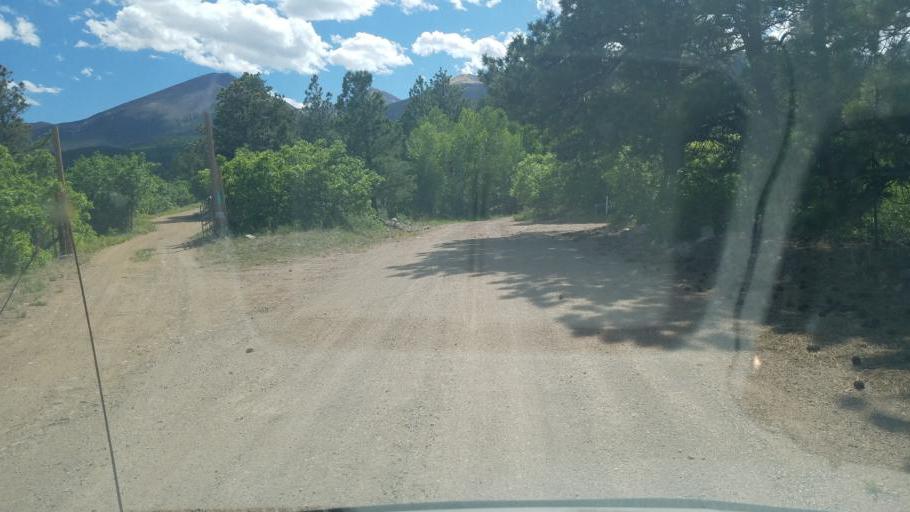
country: US
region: Colorado
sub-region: Custer County
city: Westcliffe
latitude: 38.2251
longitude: -105.6129
